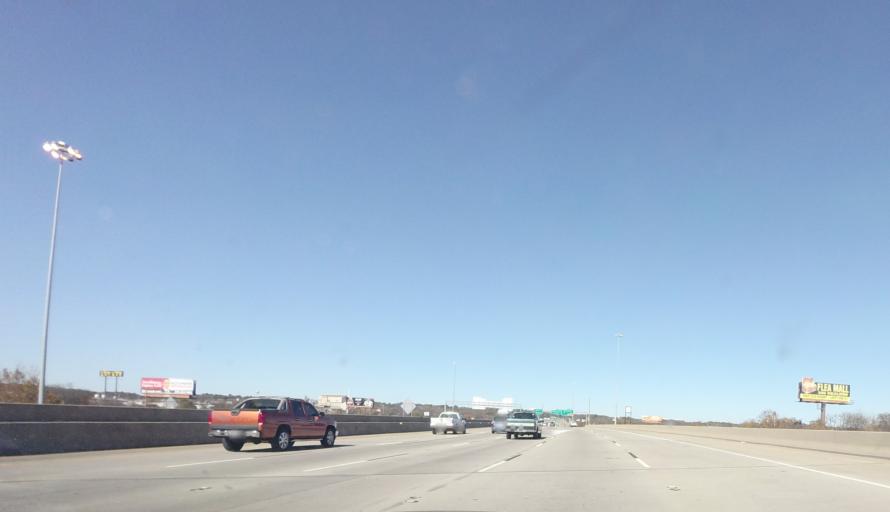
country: US
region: Alabama
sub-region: Jefferson County
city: Birmingham
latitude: 33.5371
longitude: -86.8237
